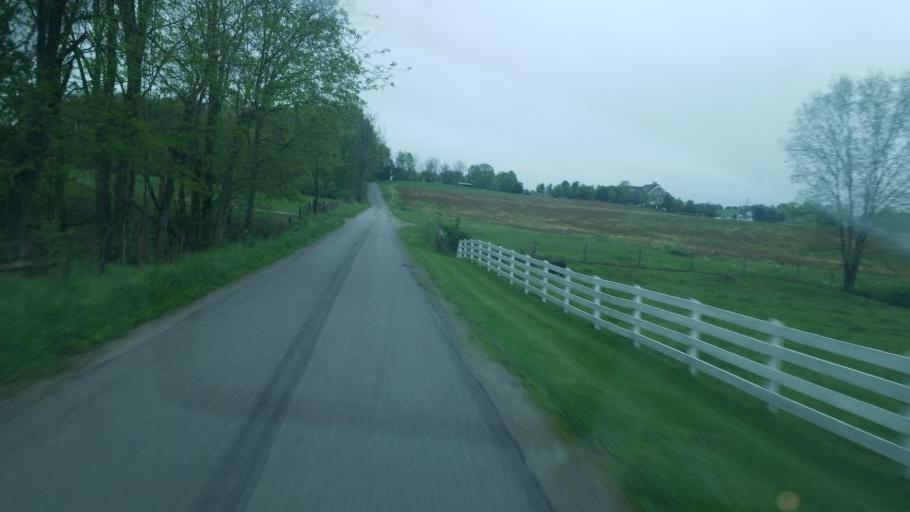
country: US
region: Ohio
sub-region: Highland County
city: Hillsboro
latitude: 39.1826
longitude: -83.6485
